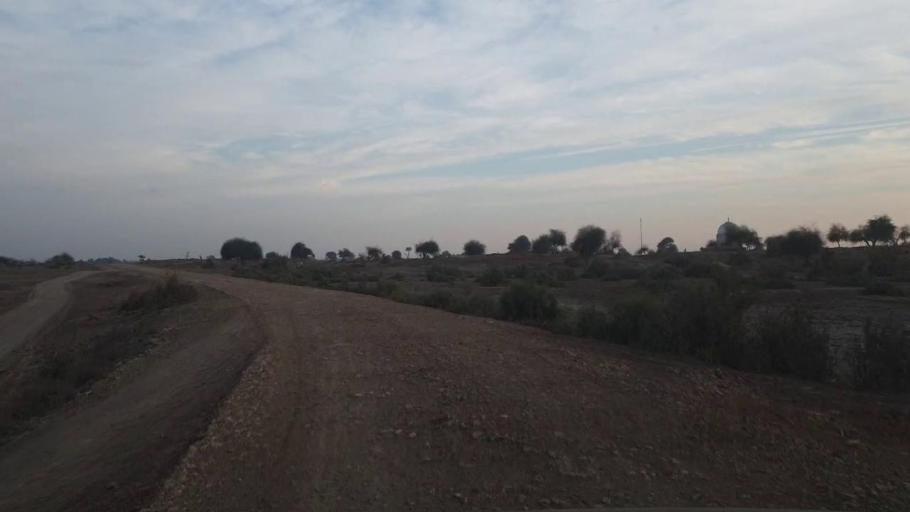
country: PK
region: Sindh
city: Shahpur Chakar
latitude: 26.0603
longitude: 68.5285
